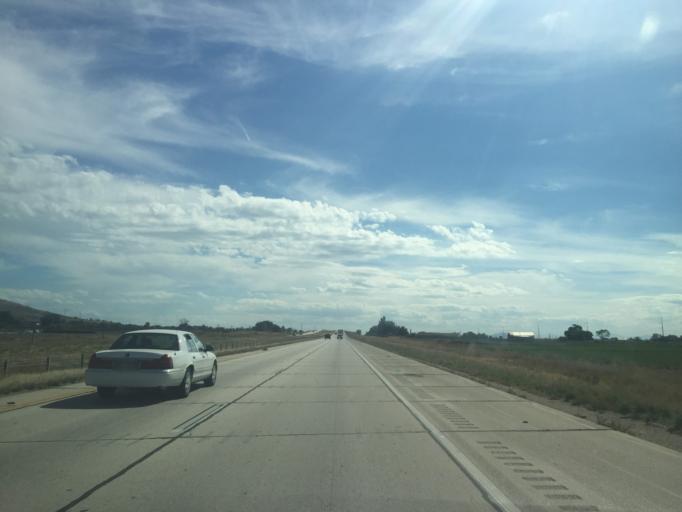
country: US
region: Utah
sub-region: Box Elder County
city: South Willard
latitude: 41.3773
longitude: -112.0426
